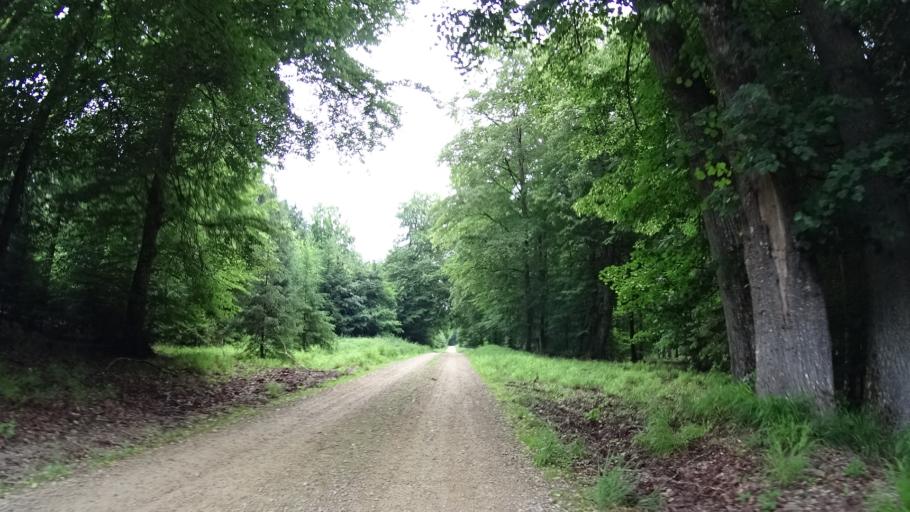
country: DE
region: Bavaria
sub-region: Upper Bavaria
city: Stammham
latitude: 48.8875
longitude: 11.5259
